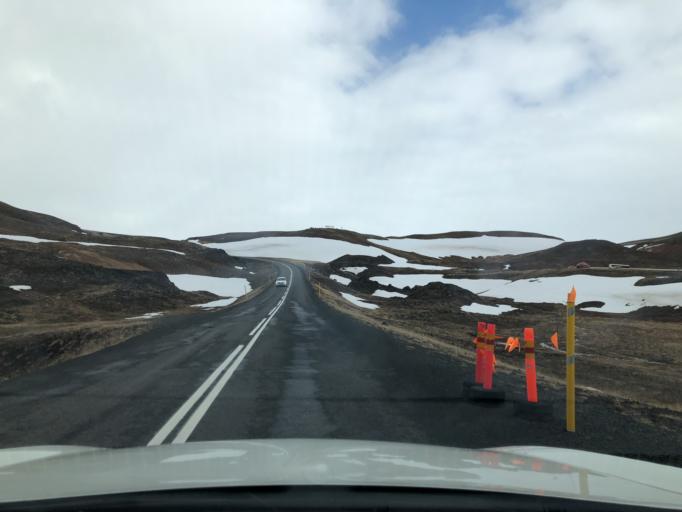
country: IS
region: Northeast
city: Laugar
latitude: 65.7069
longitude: -16.7717
